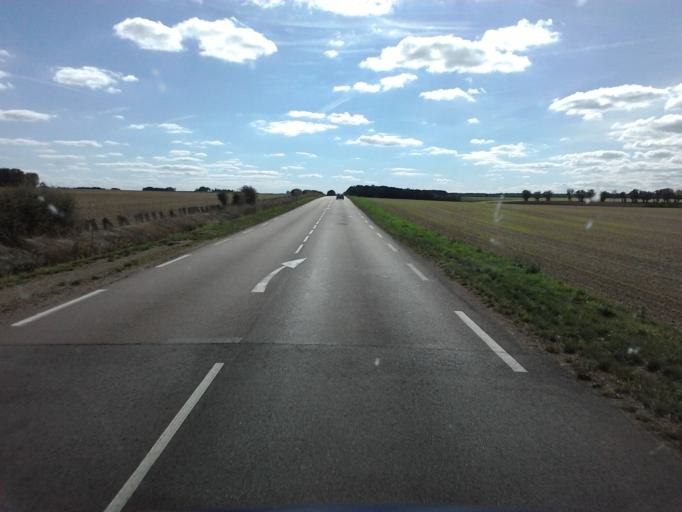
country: FR
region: Bourgogne
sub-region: Departement de la Cote-d'Or
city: Chatillon-sur-Seine
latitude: 47.8449
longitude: 4.5535
